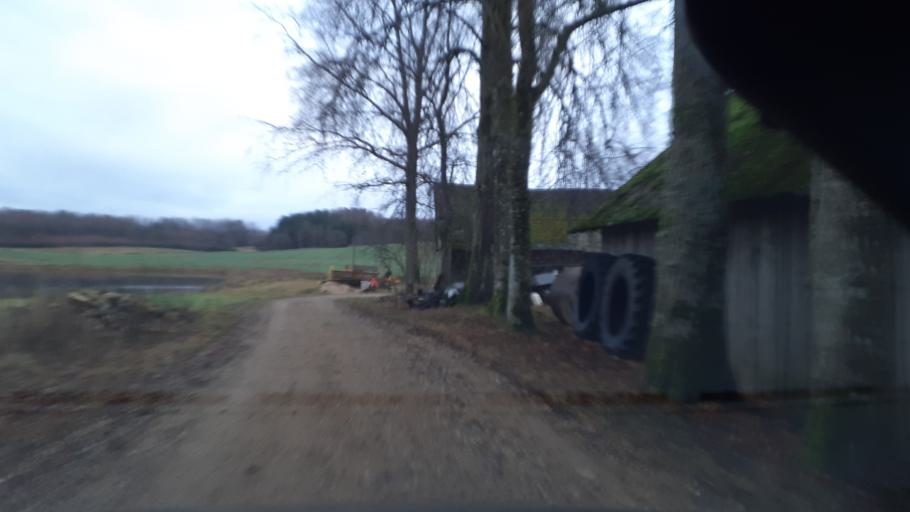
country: LV
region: Alsunga
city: Alsunga
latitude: 56.8792
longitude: 21.6860
